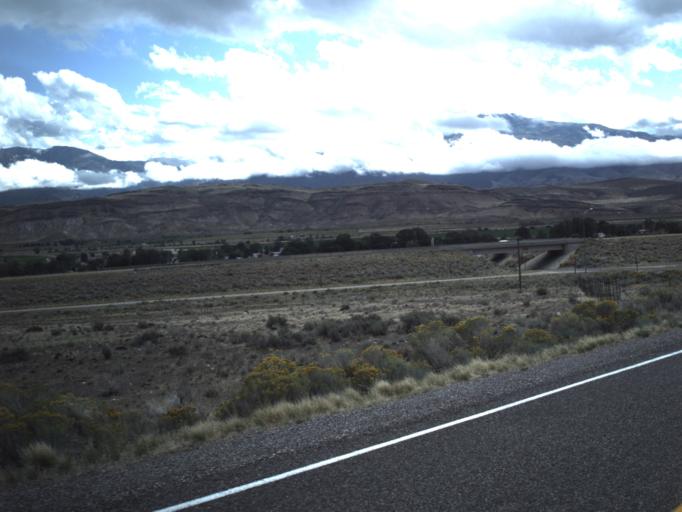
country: US
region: Utah
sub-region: Sevier County
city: Monroe
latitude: 38.6264
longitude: -112.2290
